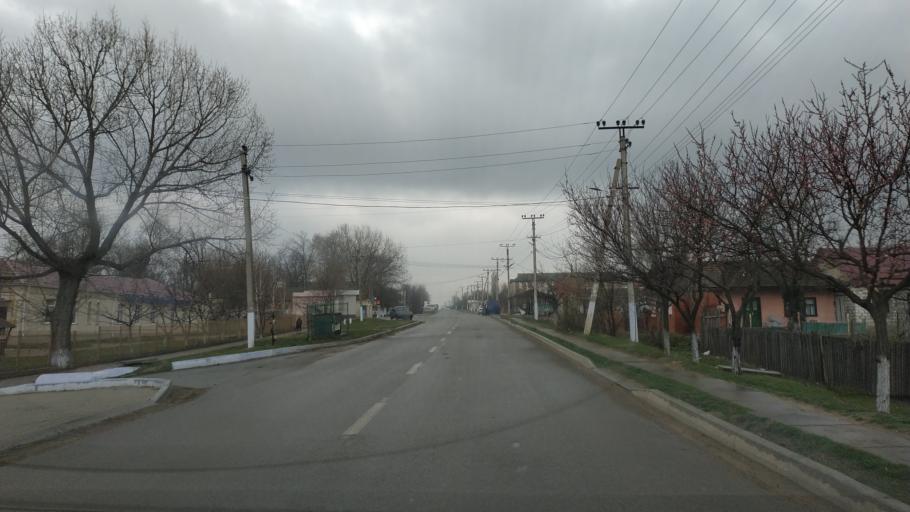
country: MD
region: Gagauzia
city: Comrat
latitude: 46.3032
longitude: 28.6391
